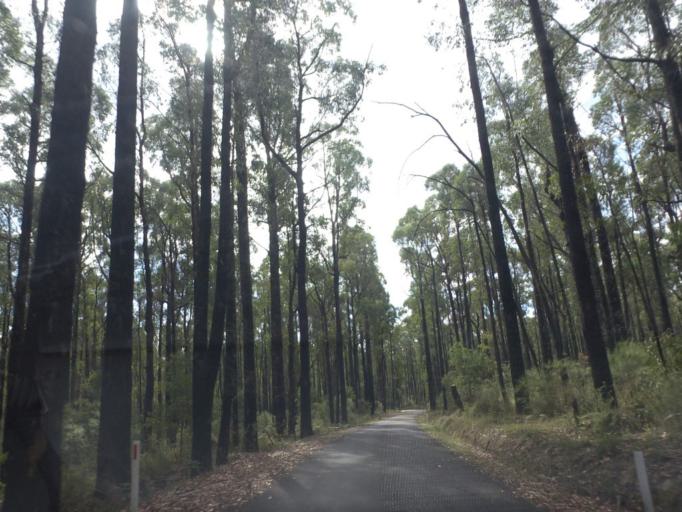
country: AU
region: Victoria
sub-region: Yarra Ranges
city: Healesville
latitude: -37.5596
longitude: 145.6778
